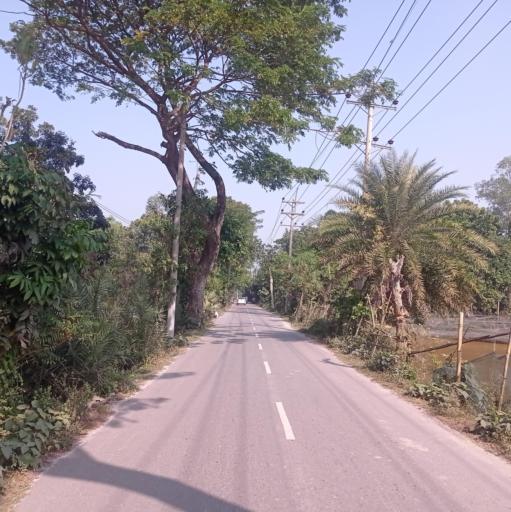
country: BD
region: Dhaka
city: Narsingdi
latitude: 24.0621
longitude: 90.6889
